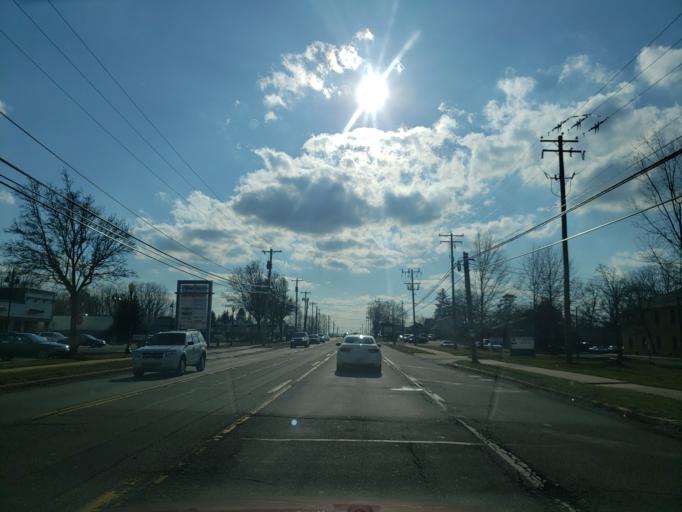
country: US
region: Pennsylvania
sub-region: Montgomery County
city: Blue Bell
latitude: 40.1552
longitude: -75.3022
